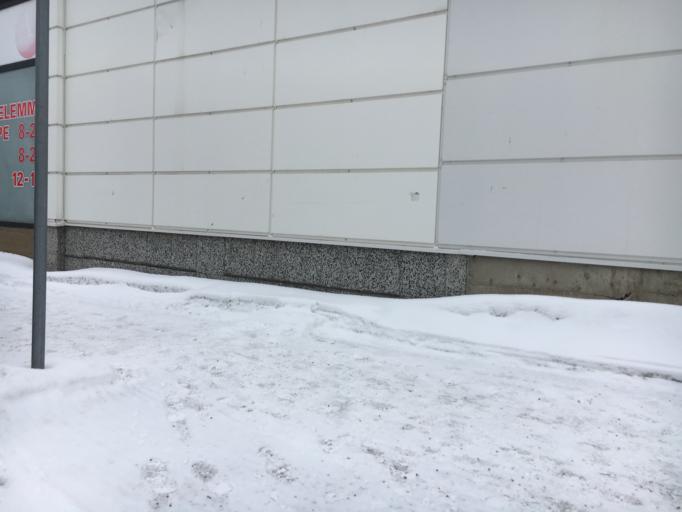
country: FI
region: Kainuu
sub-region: Kajaani
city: Kajaani
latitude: 64.2233
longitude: 27.7340
